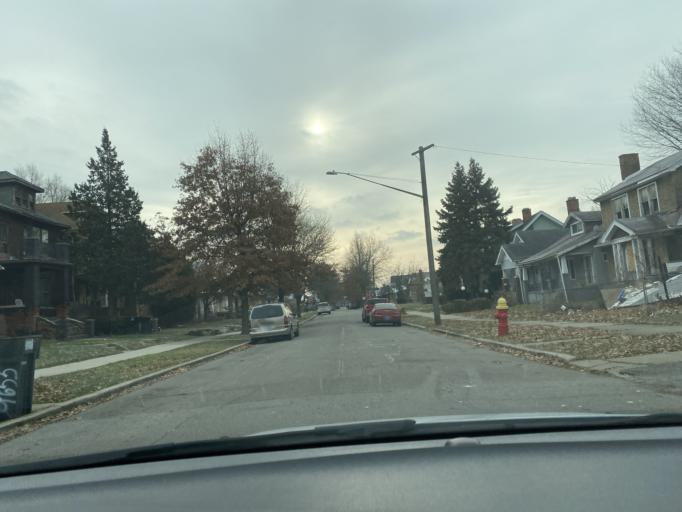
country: US
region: Michigan
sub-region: Wayne County
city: Highland Park
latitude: 42.3714
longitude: -83.1254
